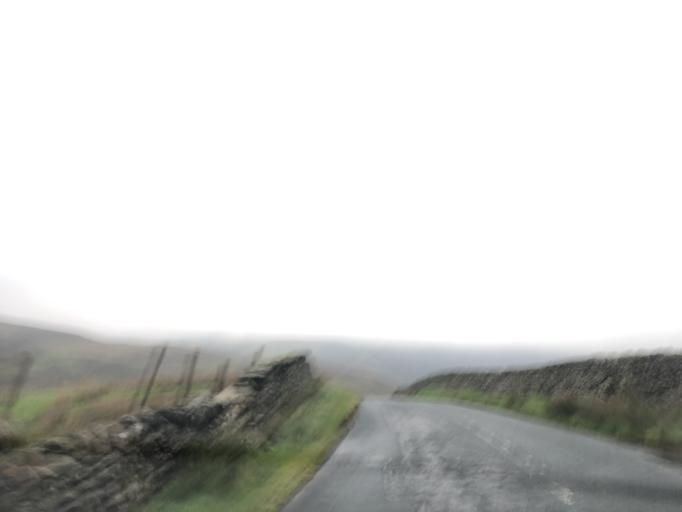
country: GB
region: England
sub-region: Cumbria
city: Ambleside
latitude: 54.4526
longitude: -2.9145
